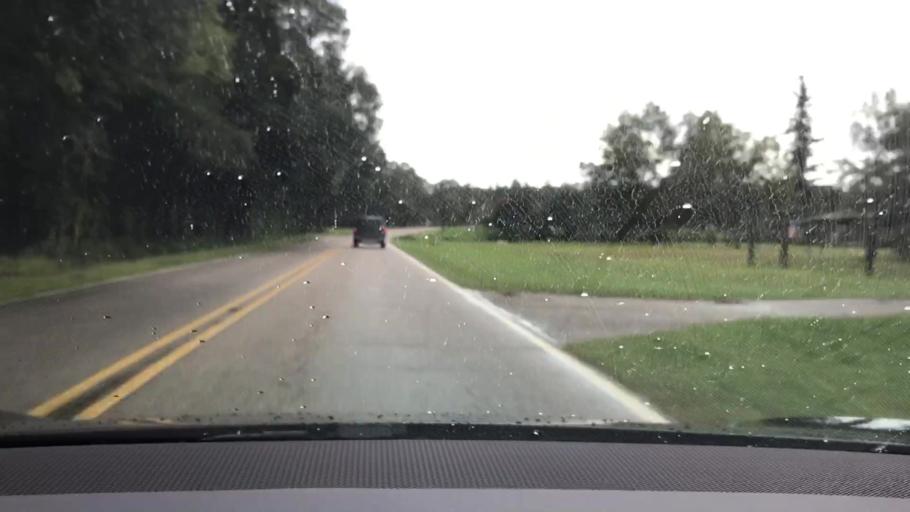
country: US
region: Alabama
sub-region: Geneva County
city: Samson
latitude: 31.1276
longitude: -86.1288
